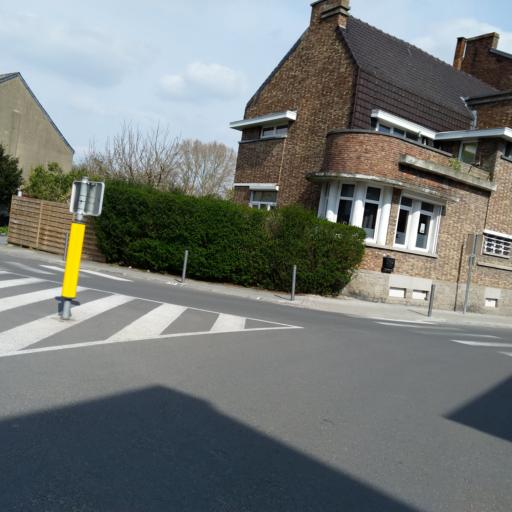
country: BE
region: Wallonia
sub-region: Province du Hainaut
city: Mons
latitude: 50.4405
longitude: 3.9624
